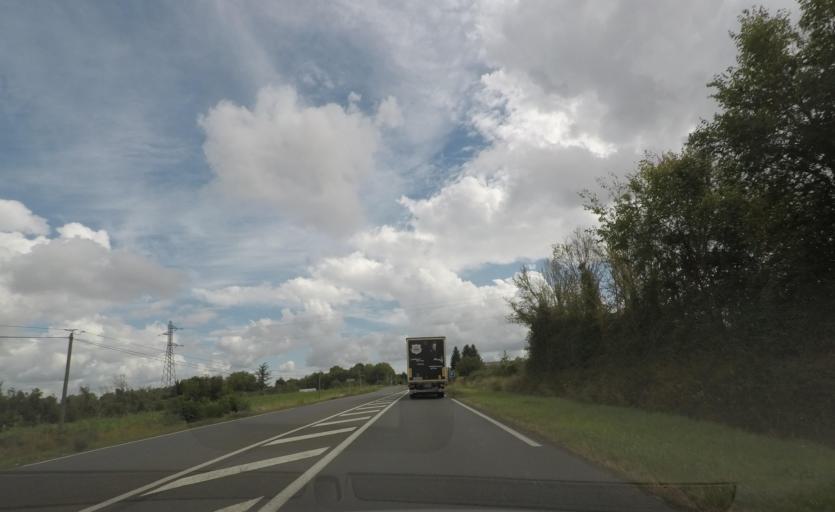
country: FR
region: Pays de la Loire
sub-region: Departement de Maine-et-Loire
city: Corze
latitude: 47.5597
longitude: -0.3741
